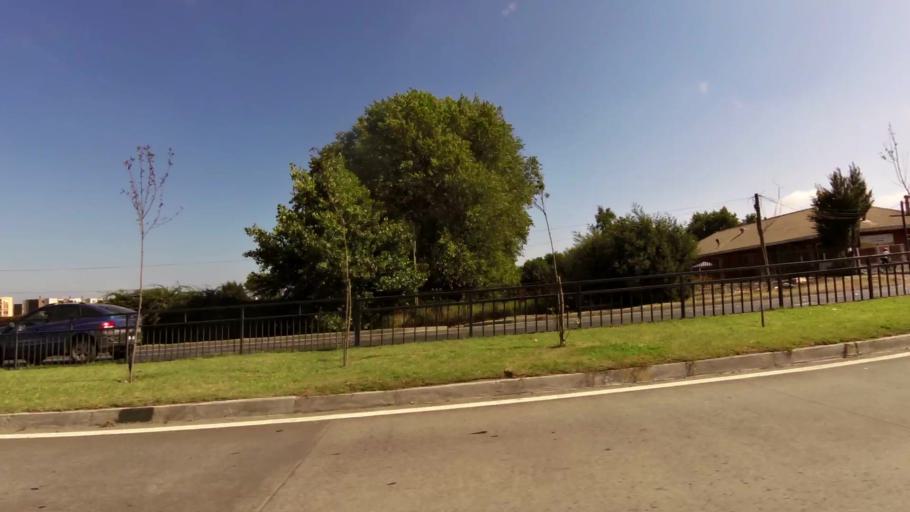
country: CL
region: Biobio
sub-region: Provincia de Concepcion
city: Concepcion
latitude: -36.7839
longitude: -73.0821
